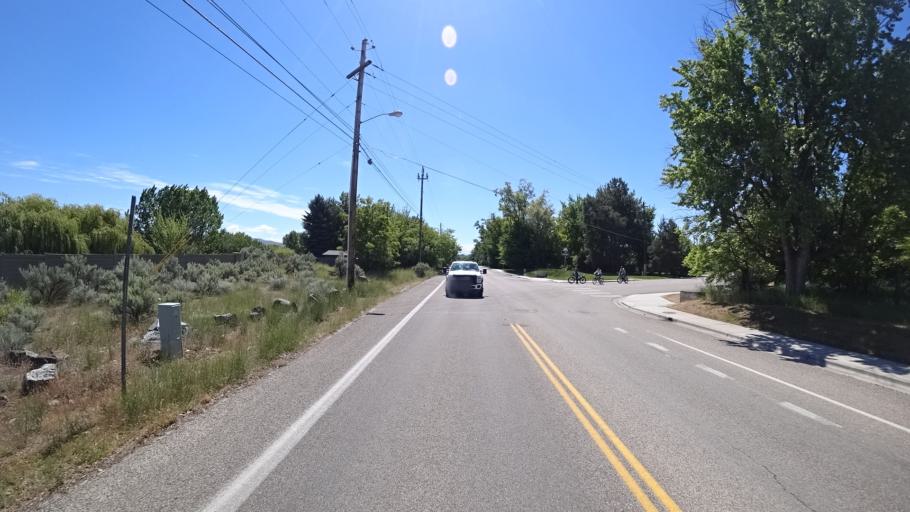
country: US
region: Idaho
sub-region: Ada County
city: Boise
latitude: 43.5716
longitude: -116.1533
